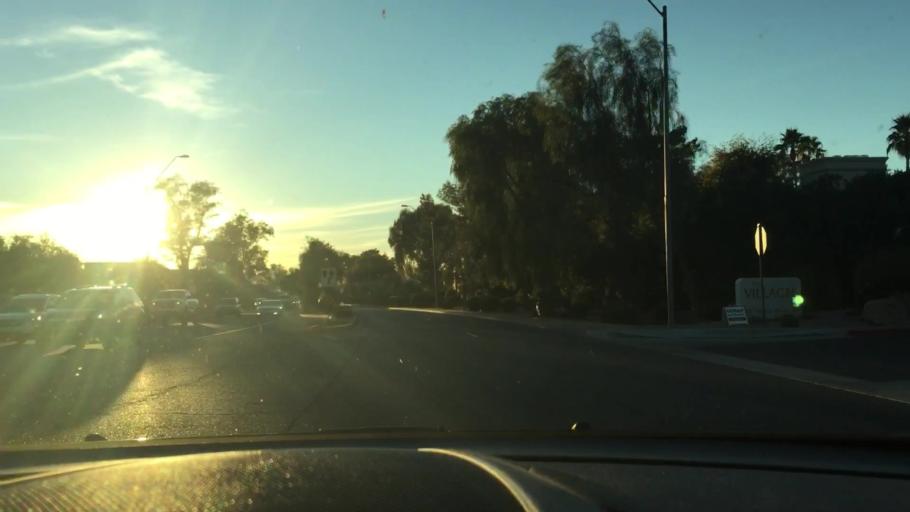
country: US
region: Arizona
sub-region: Maricopa County
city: Scottsdale
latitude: 33.5715
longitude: -111.8778
